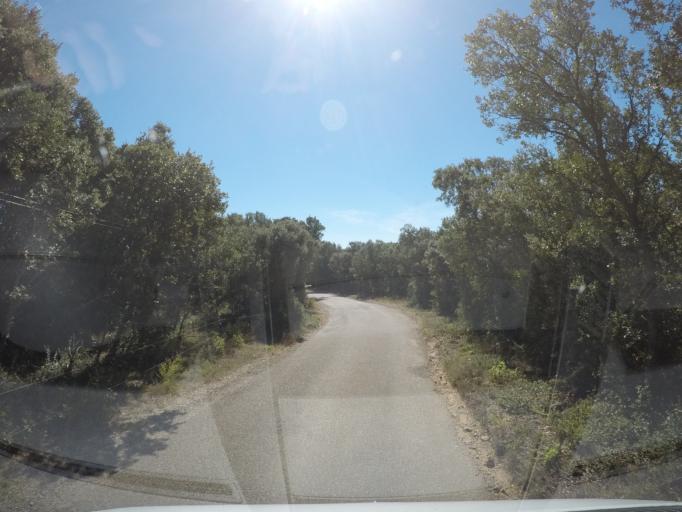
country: FR
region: Languedoc-Roussillon
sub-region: Departement de l'Herault
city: Aniane
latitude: 43.7321
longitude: 3.6505
